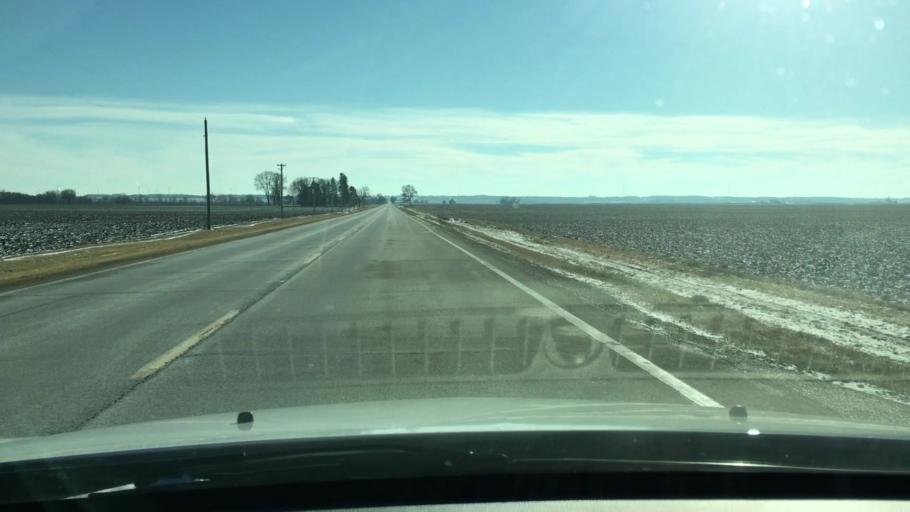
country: US
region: Illinois
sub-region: Ogle County
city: Rochelle
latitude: 41.7879
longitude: -89.0836
